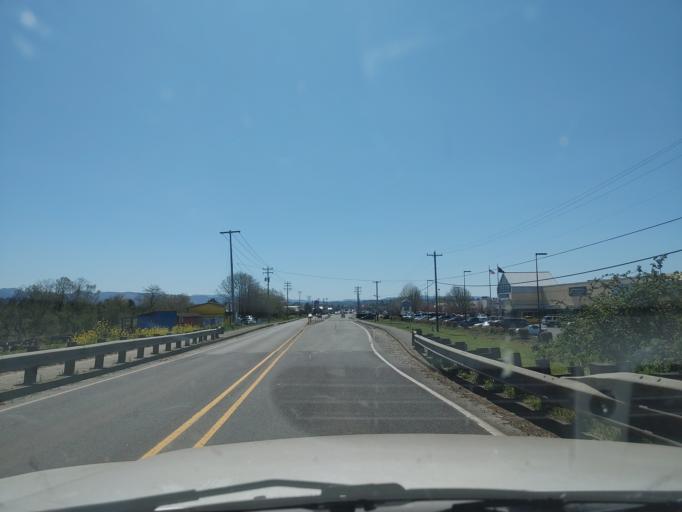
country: US
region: Oregon
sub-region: Tillamook County
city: Tillamook
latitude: 45.4782
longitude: -123.8445
